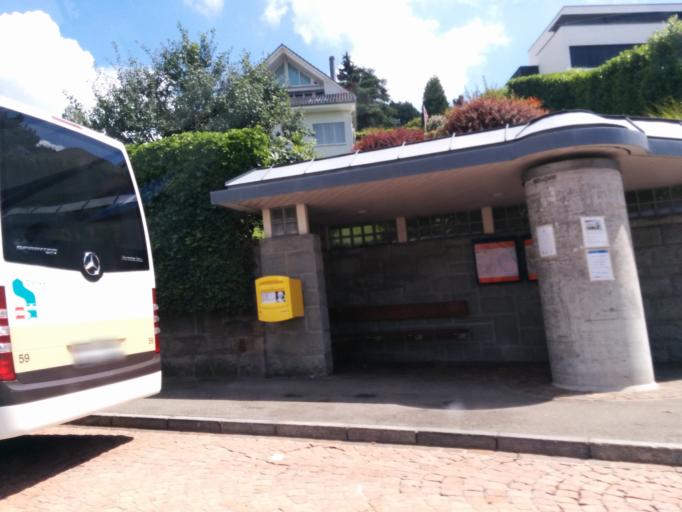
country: CH
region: Zurich
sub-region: Bezirk Meilen
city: Kuesnacht / Goldbach
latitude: 47.3261
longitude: 8.5823
